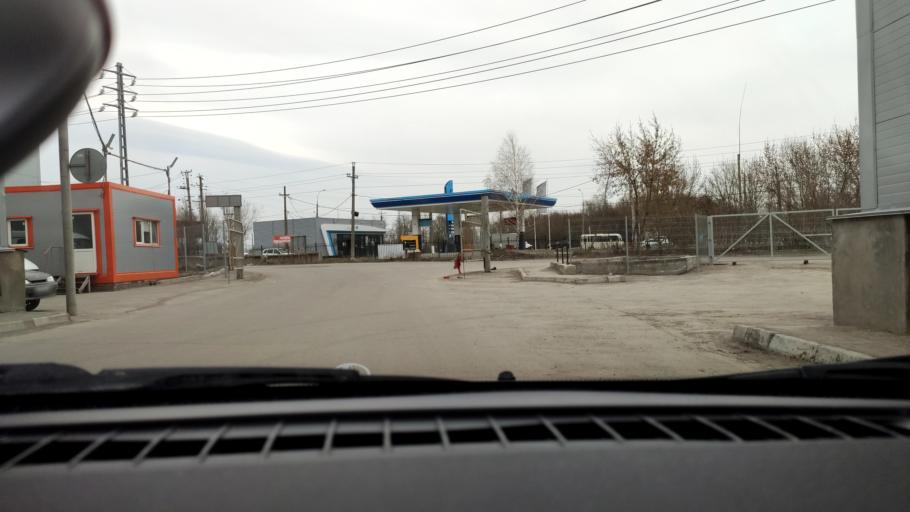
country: RU
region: Samara
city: Smyshlyayevka
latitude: 53.2573
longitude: 50.3717
